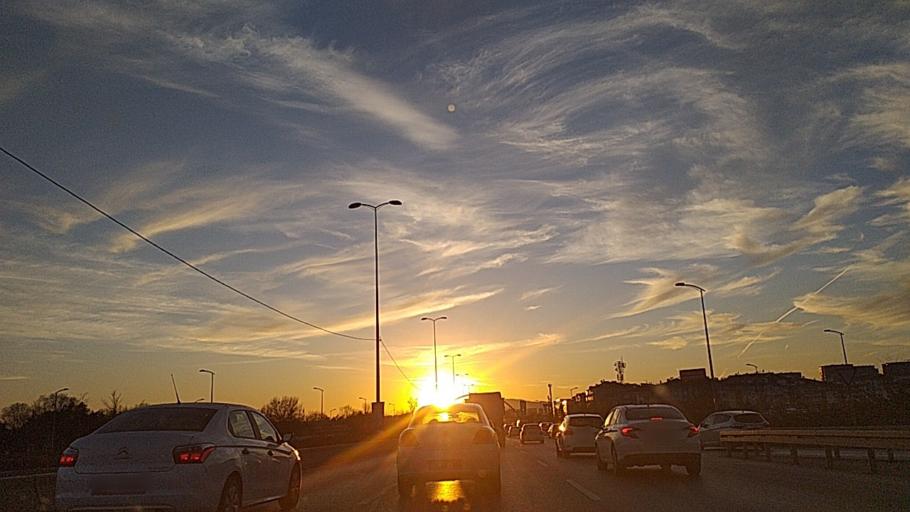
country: TR
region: Ankara
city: Etimesgut
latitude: 39.9631
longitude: 32.6683
